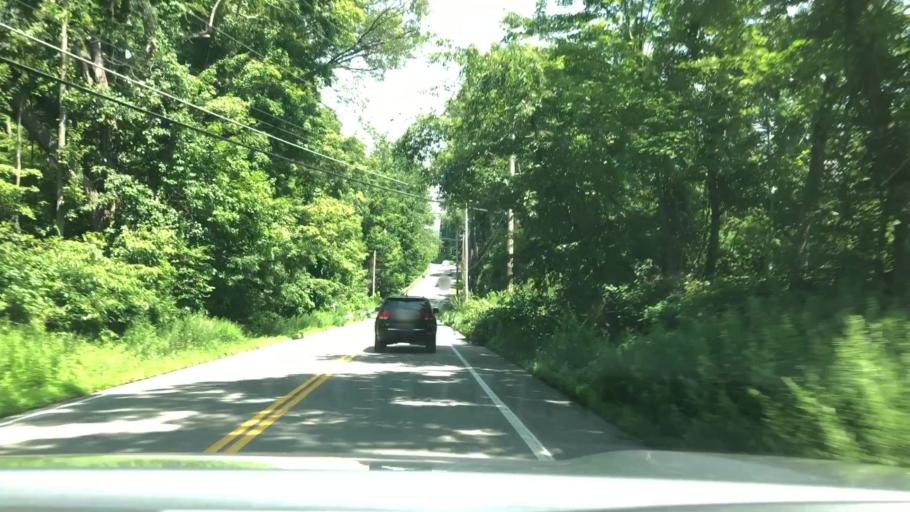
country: US
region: New York
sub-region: Orange County
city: Highland Falls
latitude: 41.3663
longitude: -73.9492
